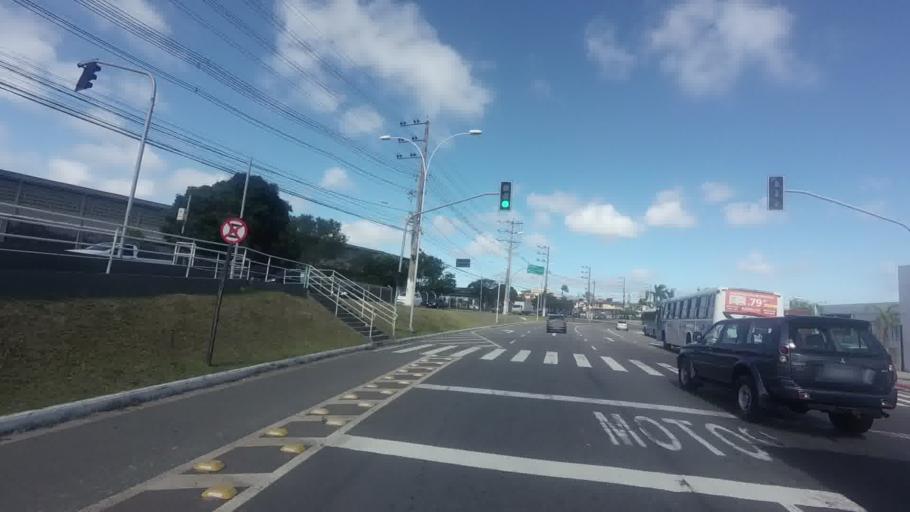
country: BR
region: Espirito Santo
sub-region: Vila Velha
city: Vila Velha
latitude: -20.2393
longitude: -40.2746
